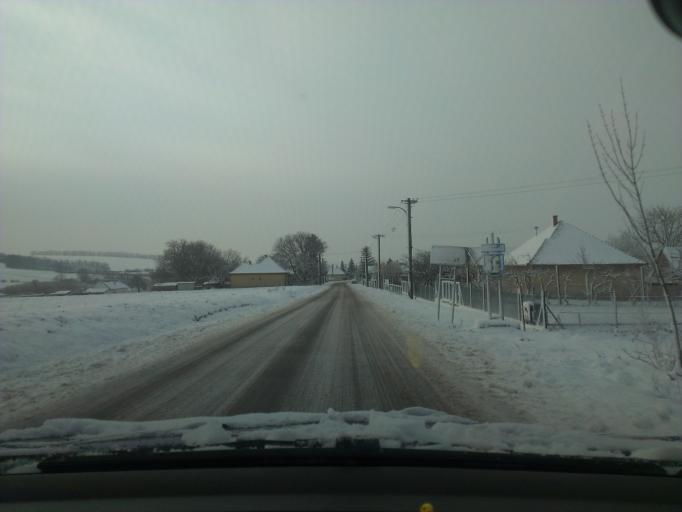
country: SK
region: Trnavsky
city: Hlohovec
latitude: 48.4808
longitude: 17.9888
